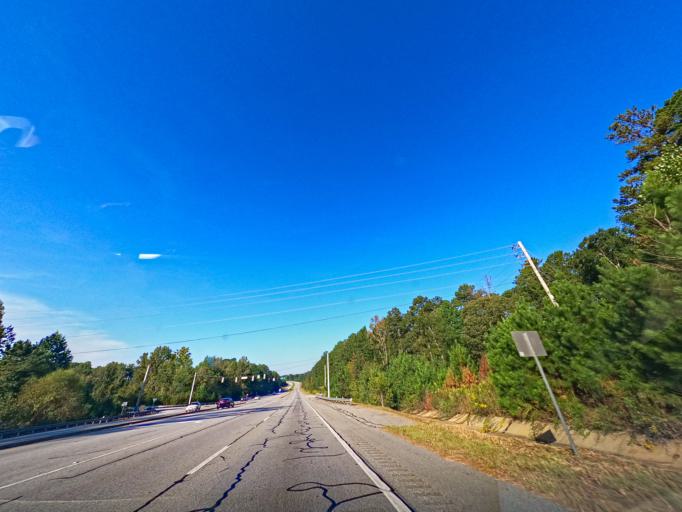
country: US
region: Georgia
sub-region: Coweta County
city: Newnan
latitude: 33.3990
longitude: -84.8127
